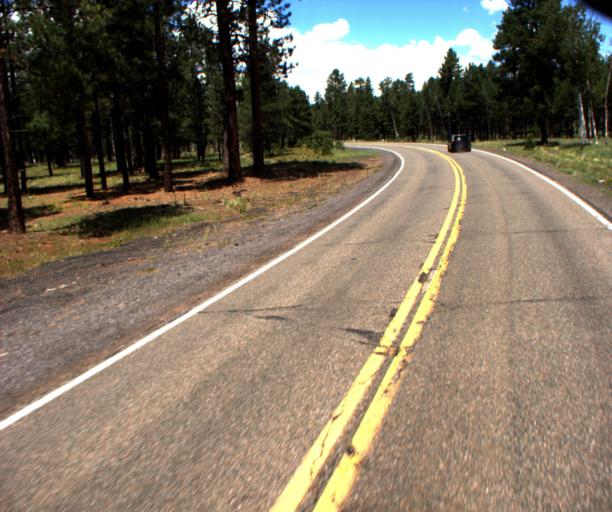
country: US
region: Arizona
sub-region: Coconino County
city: Flagstaff
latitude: 35.3242
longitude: -111.7729
